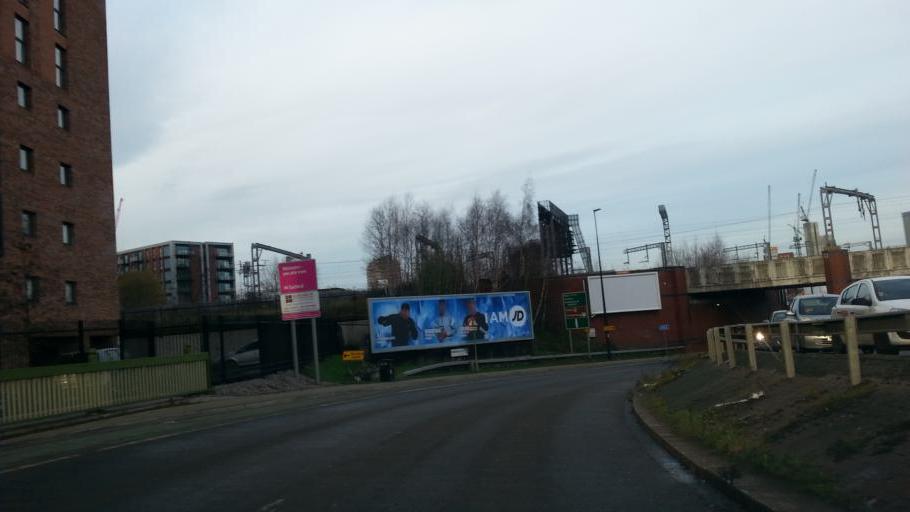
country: GB
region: England
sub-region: Manchester
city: Hulme
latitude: 53.4775
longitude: -2.2617
